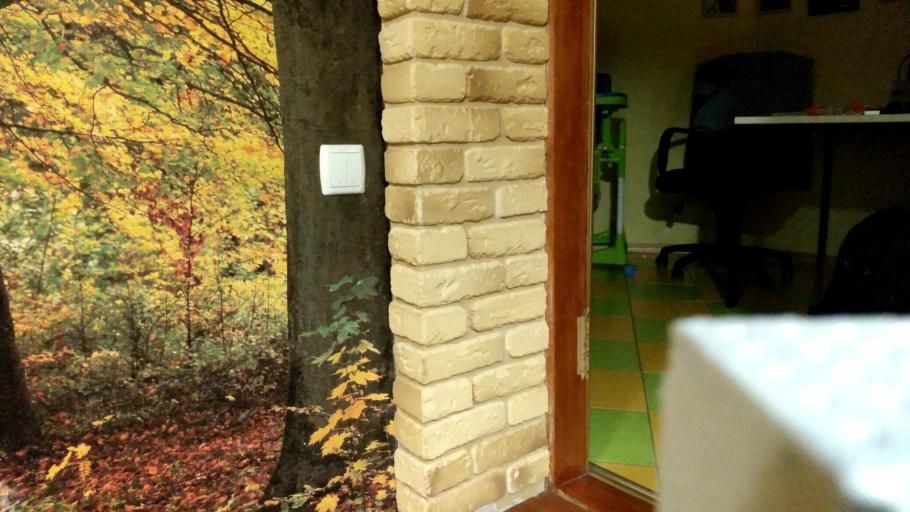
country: RU
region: Arkhangelskaya
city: Kargopol'
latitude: 61.5717
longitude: 37.7543
